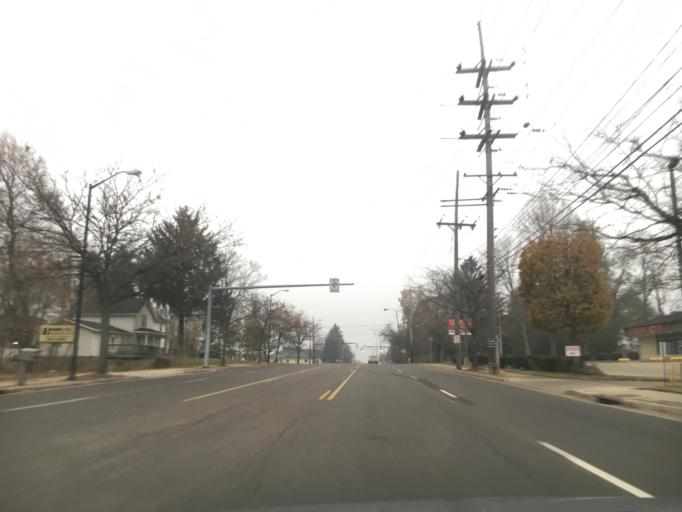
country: US
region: Ohio
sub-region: Summit County
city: Cuyahoga Falls
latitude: 41.1128
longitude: -81.4861
